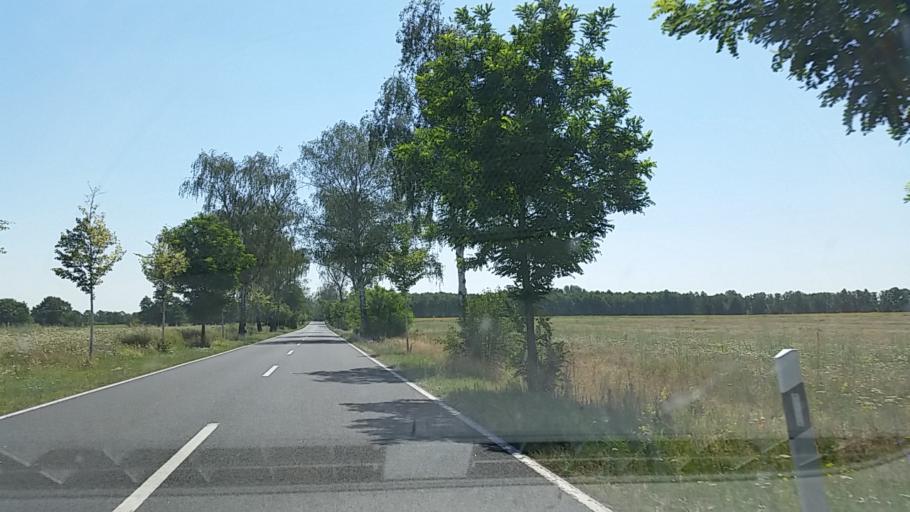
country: DE
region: Saxony-Anhalt
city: Pretzsch
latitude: 51.6775
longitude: 12.8162
